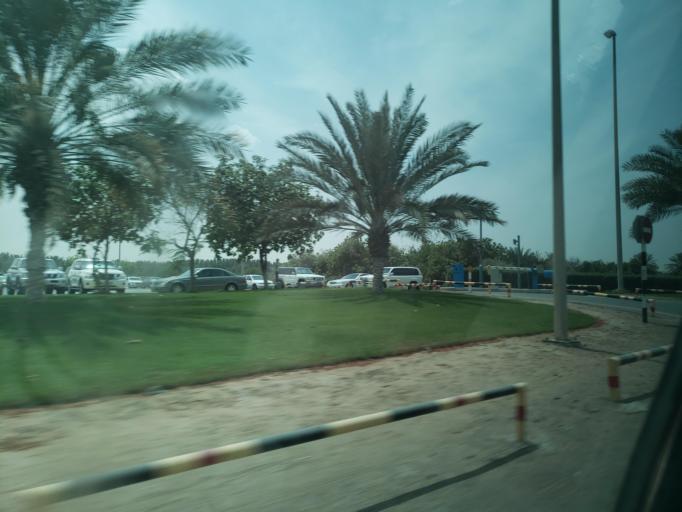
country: AE
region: Ash Shariqah
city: Sharjah
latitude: 25.3217
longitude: 55.5151
